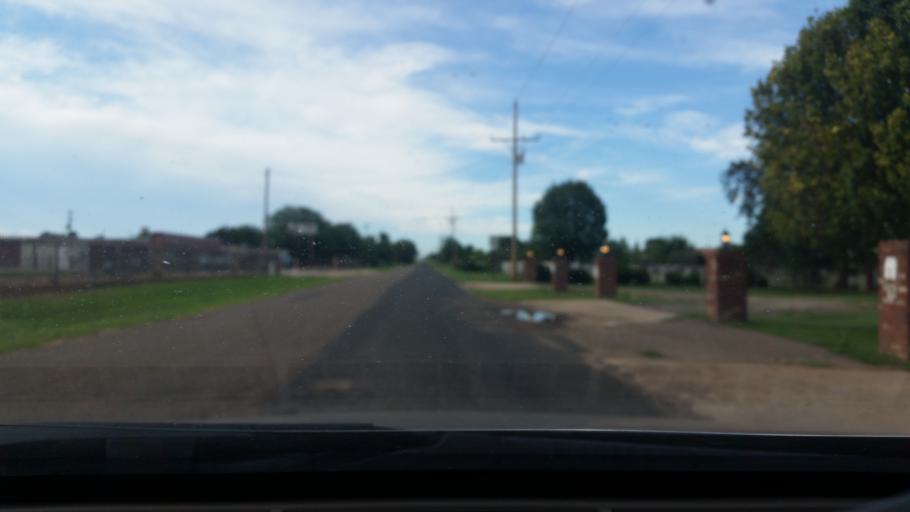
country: US
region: New Mexico
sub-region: Curry County
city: Clovis
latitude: 34.4490
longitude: -103.1784
